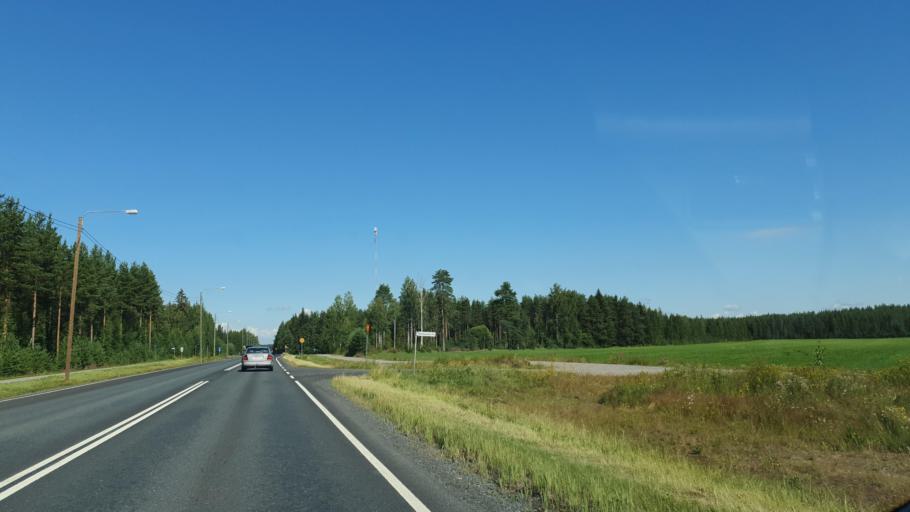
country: FI
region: Northern Savo
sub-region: Ylae-Savo
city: Lapinlahti
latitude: 63.4235
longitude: 27.3303
